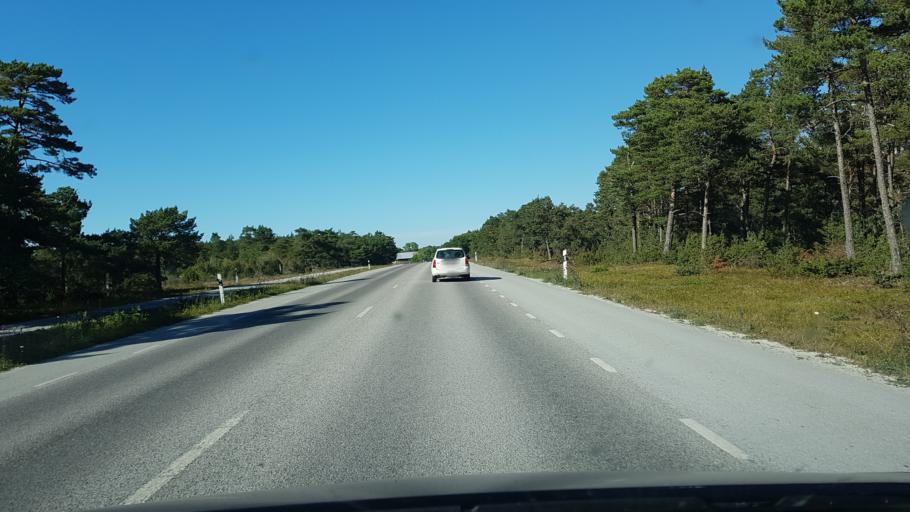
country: SE
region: Gotland
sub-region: Gotland
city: Vibble
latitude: 57.5652
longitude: 18.2062
